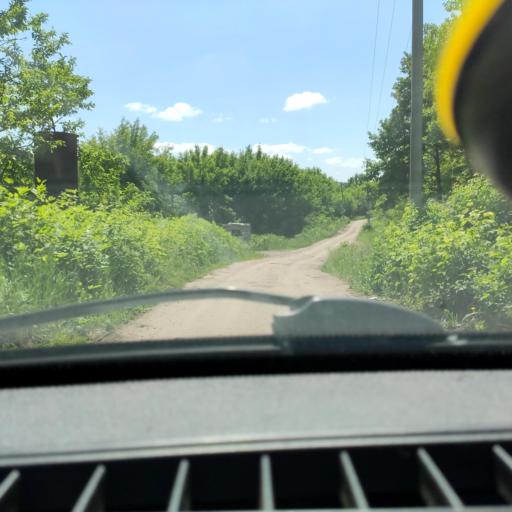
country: RU
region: Samara
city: Zhigulevsk
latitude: 53.3794
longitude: 49.5085
